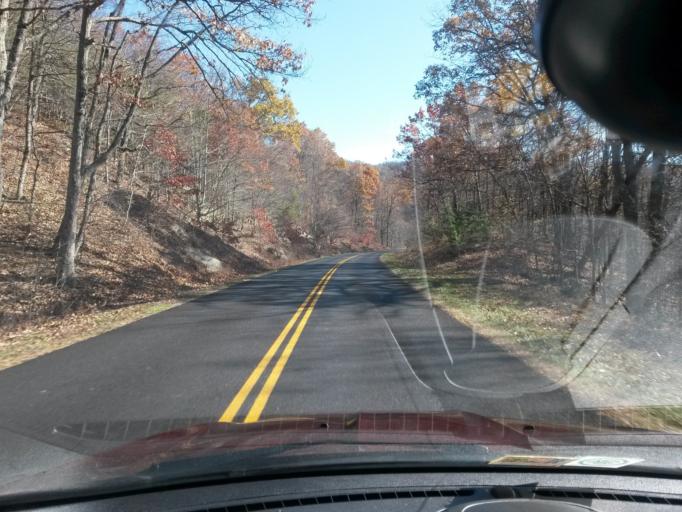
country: US
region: Virginia
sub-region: Botetourt County
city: Buchanan
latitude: 37.4811
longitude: -79.6604
